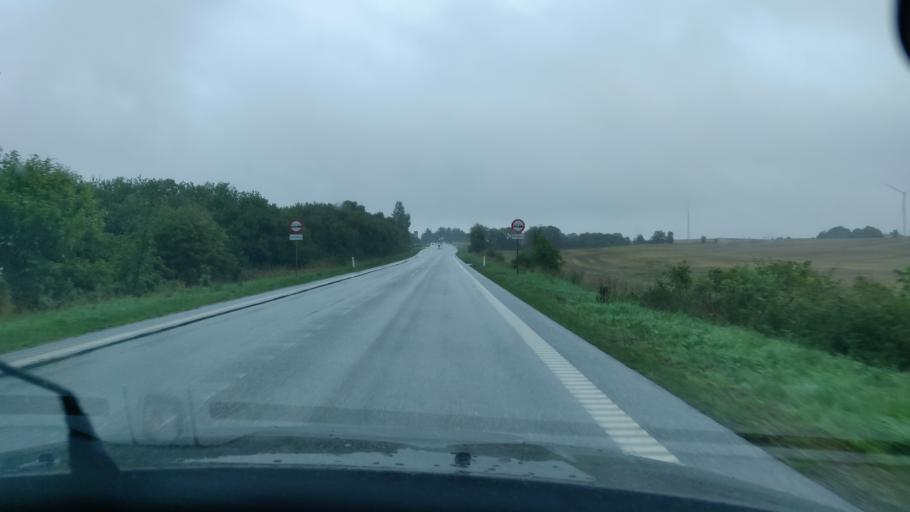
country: DK
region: North Denmark
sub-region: Thisted Kommune
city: Hurup
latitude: 56.8435
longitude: 8.5276
